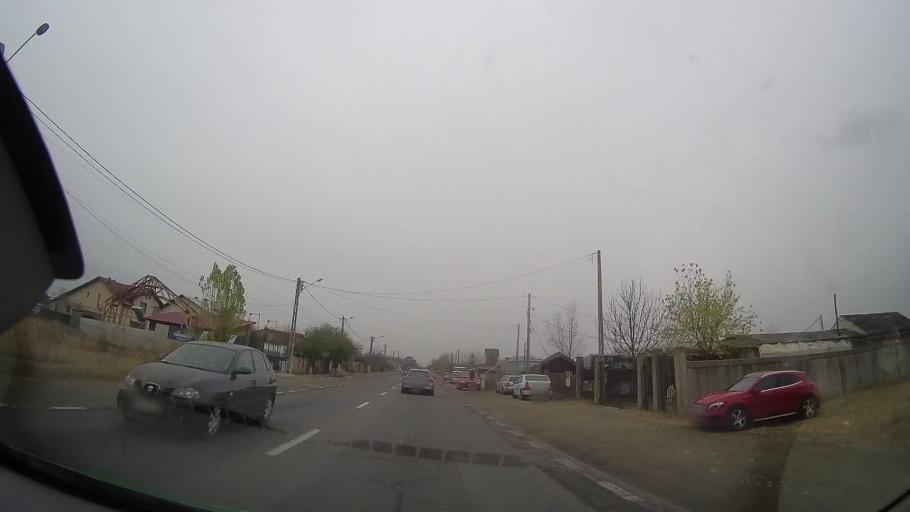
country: RO
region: Prahova
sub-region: Comuna Blejoiu
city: Ploiestiori
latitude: 44.9728
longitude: 26.0207
